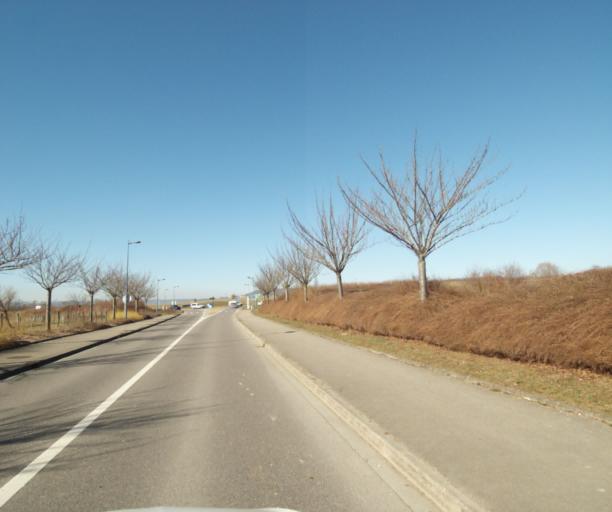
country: FR
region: Lorraine
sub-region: Departement de Meurthe-et-Moselle
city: Saulxures-les-Nancy
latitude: 48.6849
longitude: 6.2321
